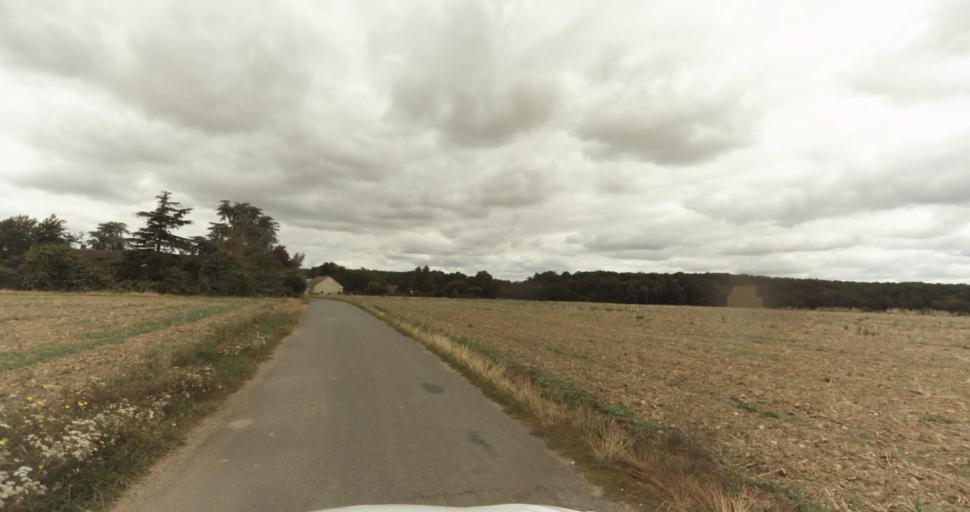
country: FR
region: Haute-Normandie
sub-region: Departement de l'Eure
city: Nonancourt
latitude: 48.8111
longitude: 1.1729
